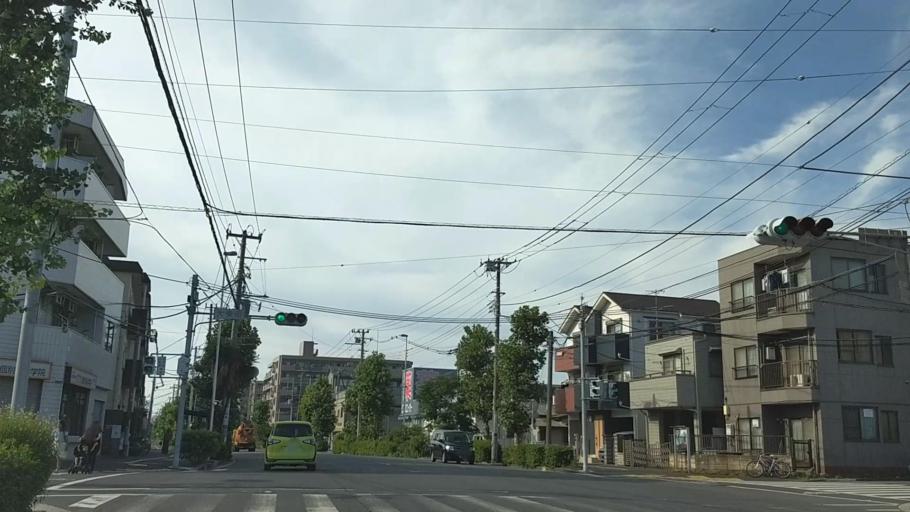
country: JP
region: Kanagawa
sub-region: Kawasaki-shi
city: Kawasaki
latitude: 35.5029
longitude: 139.6941
